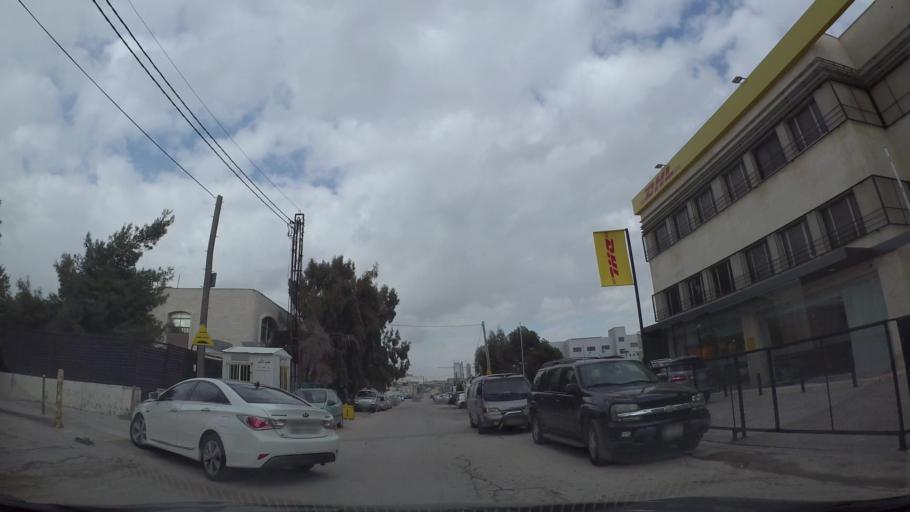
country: JO
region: Amman
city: Wadi as Sir
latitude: 31.9394
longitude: 35.8448
